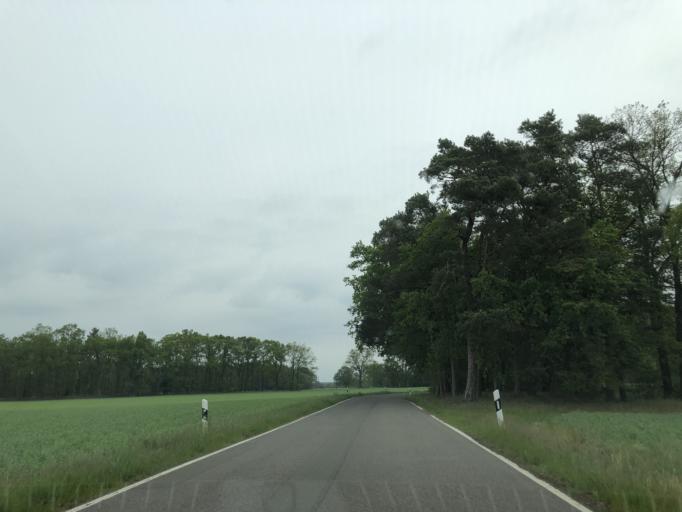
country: DE
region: Brandenburg
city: Plattenburg
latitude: 52.9509
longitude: 12.1209
